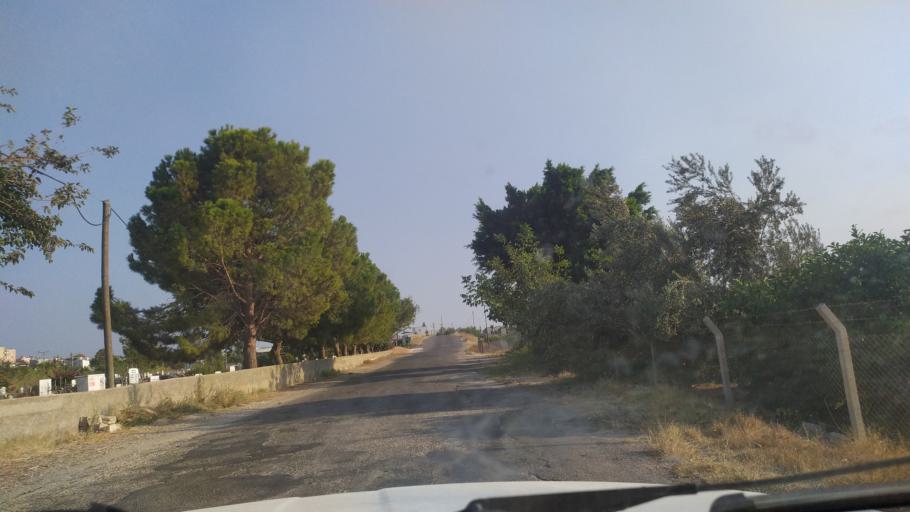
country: TR
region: Mersin
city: Silifke
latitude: 36.4007
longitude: 33.9265
